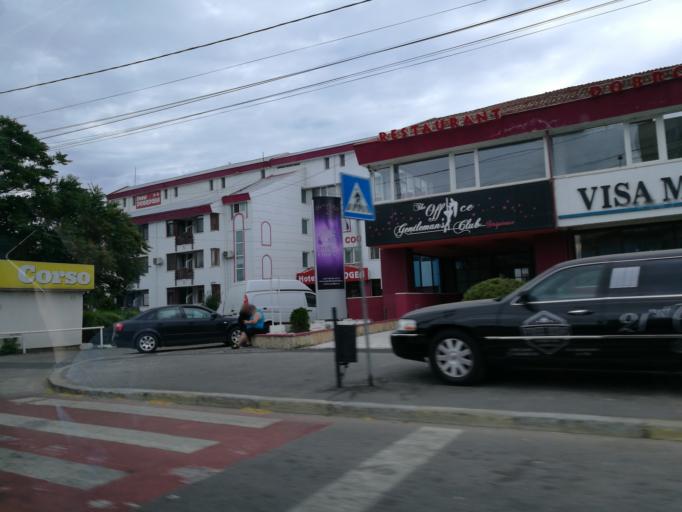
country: RO
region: Constanta
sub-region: Municipiul Constanta
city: Palazu Mare
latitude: 44.2157
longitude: 28.6284
